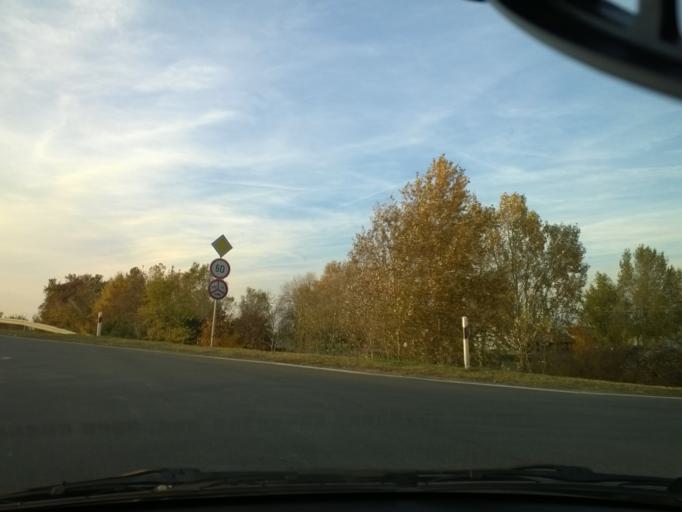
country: HU
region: Bacs-Kiskun
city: Lajosmizse
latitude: 46.9896
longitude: 19.6112
